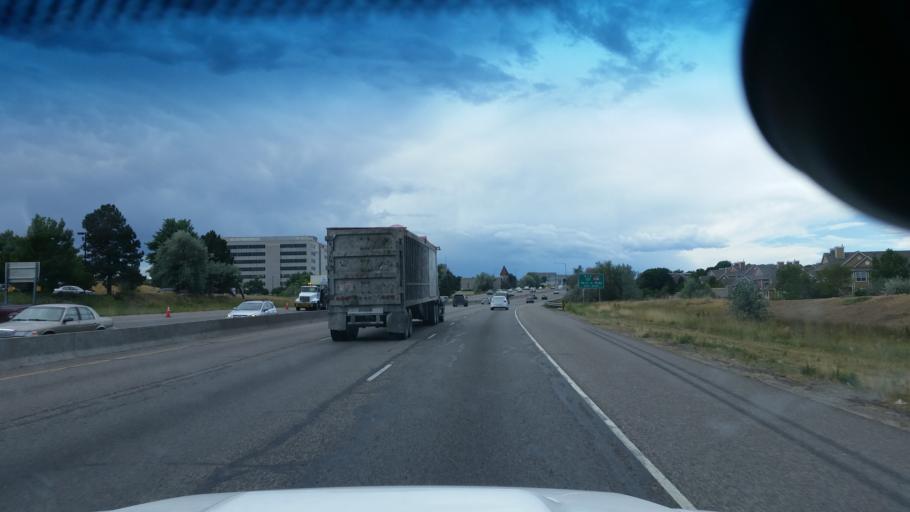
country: US
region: Colorado
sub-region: Adams County
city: Northglenn
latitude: 39.9212
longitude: -104.9878
